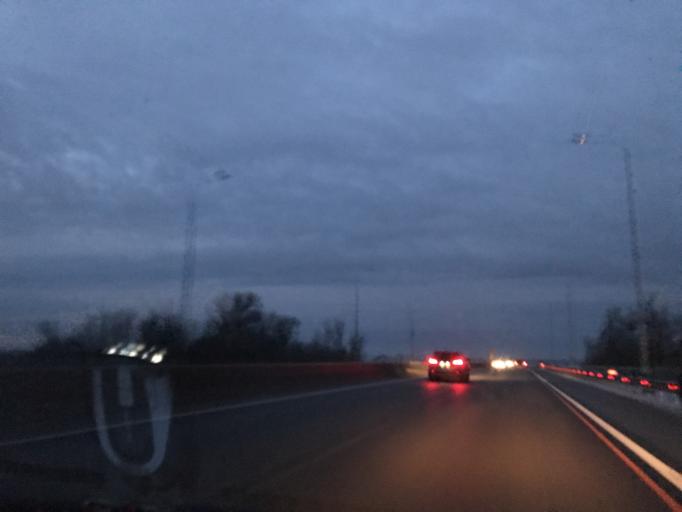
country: RU
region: Rostov
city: Samarskoye
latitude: 47.0184
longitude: 39.7356
